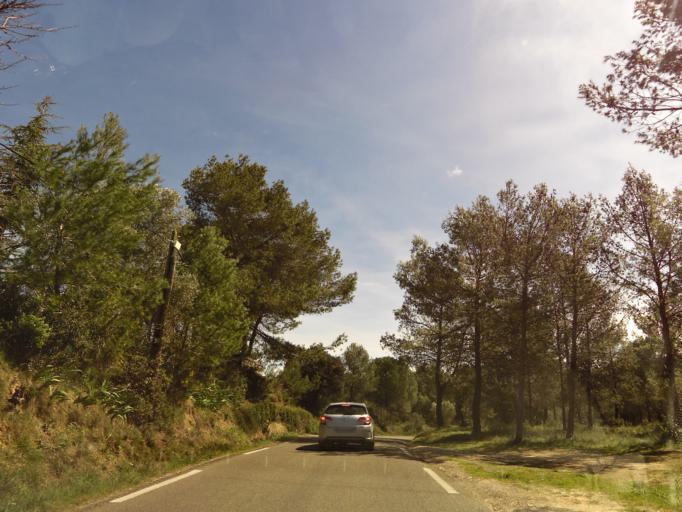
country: FR
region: Languedoc-Roussillon
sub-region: Departement du Gard
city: Bernis
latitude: 43.7792
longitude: 4.2763
